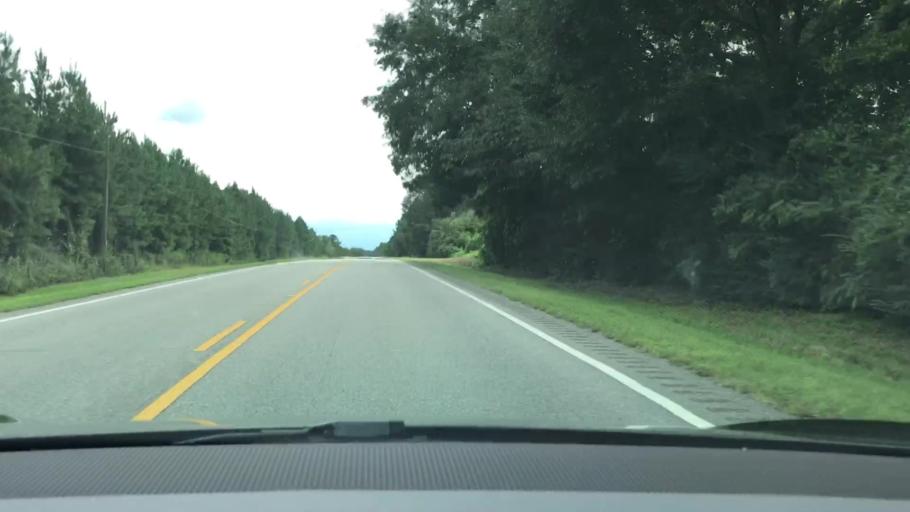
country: US
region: Alabama
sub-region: Pike County
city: Troy
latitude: 31.6313
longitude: -85.9743
